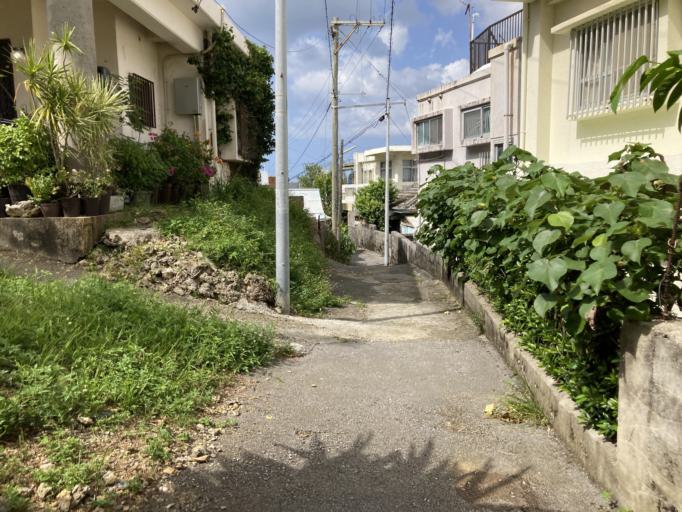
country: JP
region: Okinawa
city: Naha-shi
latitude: 26.2012
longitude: 127.6714
